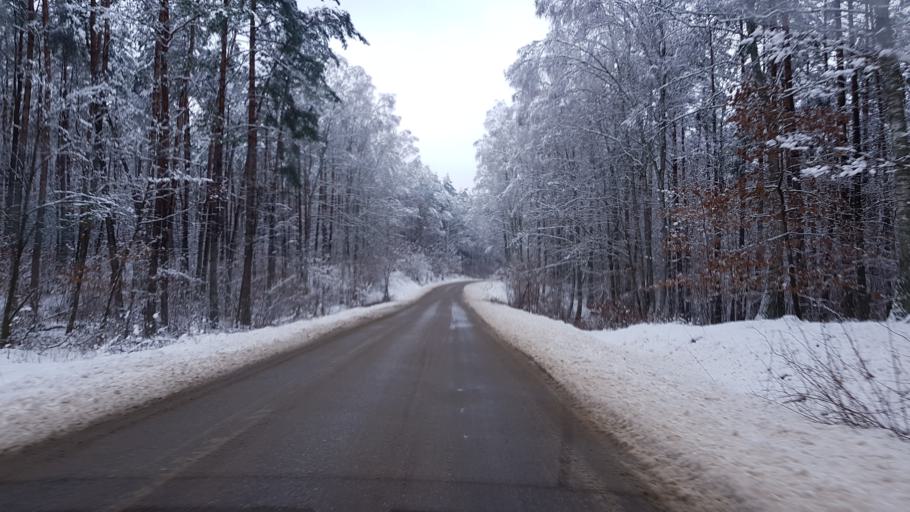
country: PL
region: West Pomeranian Voivodeship
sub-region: Powiat drawski
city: Zlocieniec
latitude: 53.5155
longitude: 16.0050
